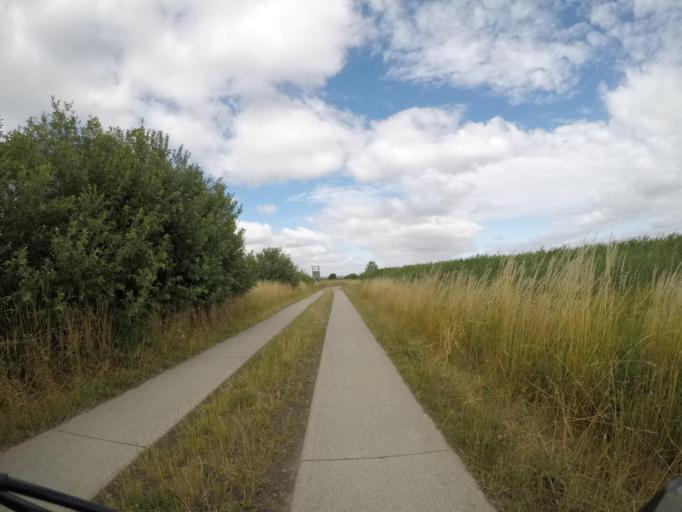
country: DE
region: Lower Saxony
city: Hitzacker
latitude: 53.1716
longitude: 11.0535
